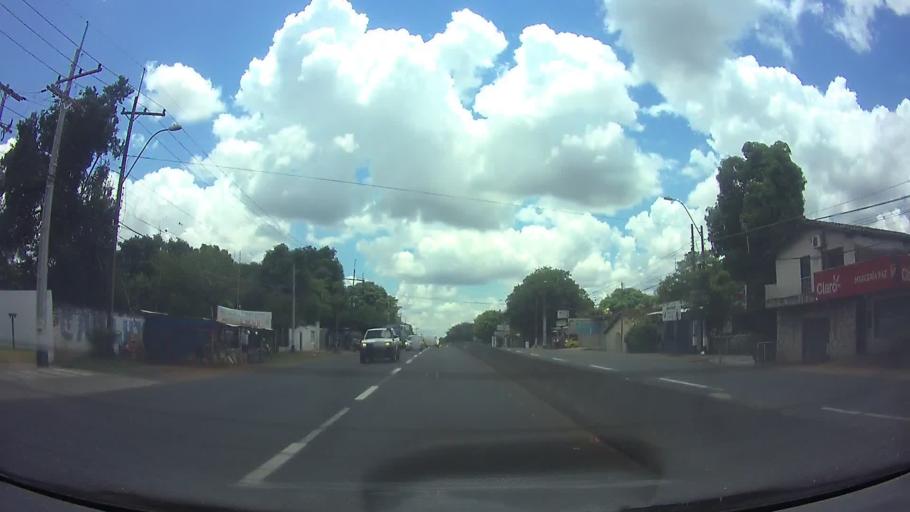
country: PY
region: Central
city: Capiata
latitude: -25.3702
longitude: -57.4167
